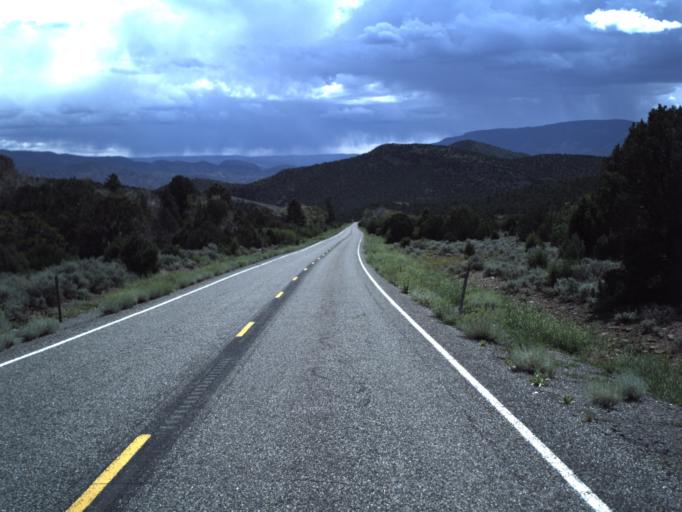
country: US
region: Utah
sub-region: Piute County
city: Junction
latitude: 38.2631
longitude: -112.2988
